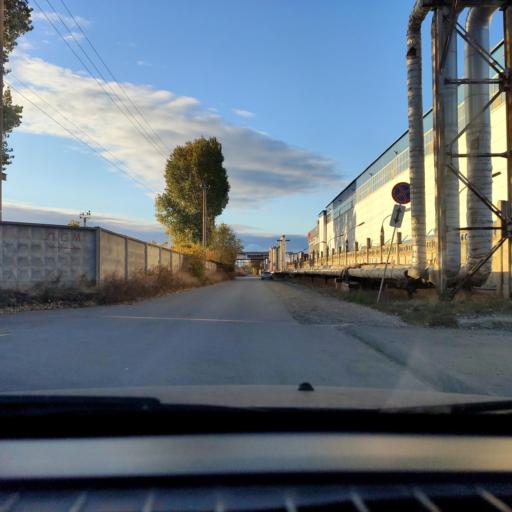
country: RU
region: Samara
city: Tol'yatti
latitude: 53.5784
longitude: 49.2634
